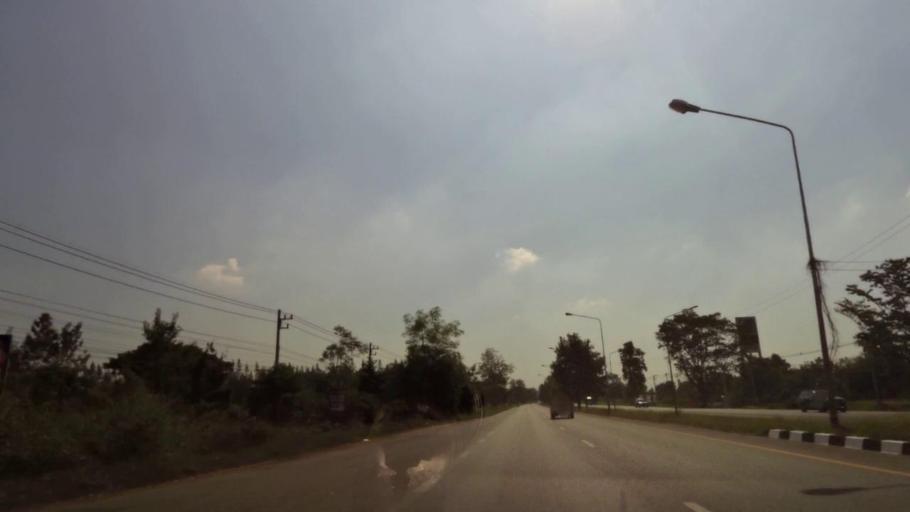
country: TH
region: Phichit
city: Bueng Na Rang
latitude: 16.1859
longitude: 100.1287
